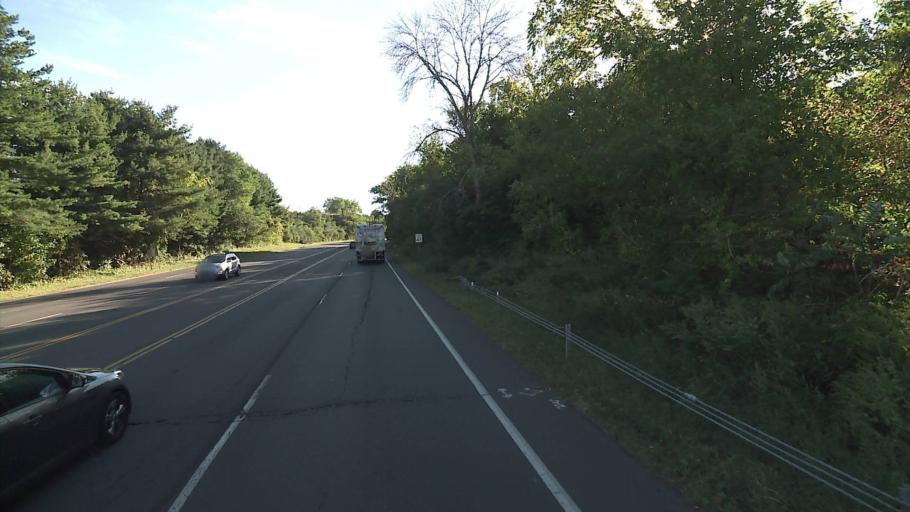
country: US
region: Connecticut
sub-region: New Haven County
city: Wallingford
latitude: 41.4826
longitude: -72.7889
